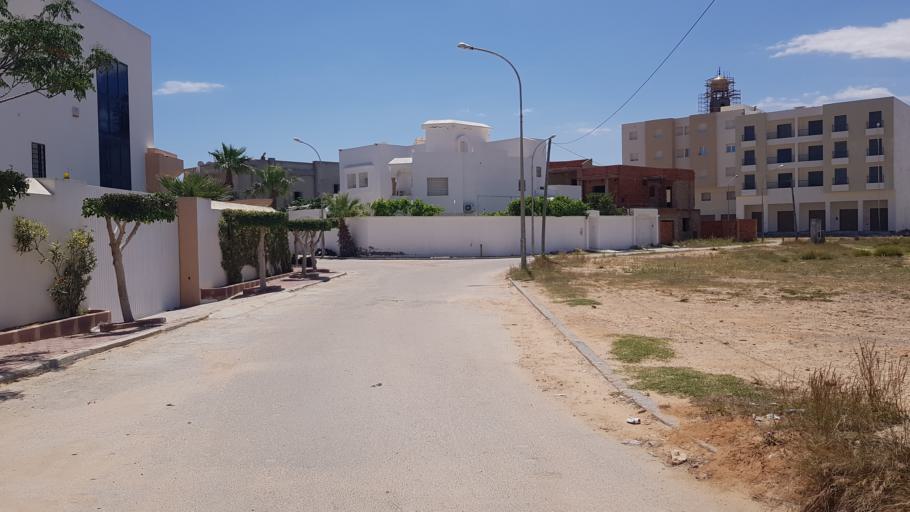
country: TN
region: Safaqis
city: Al Qarmadah
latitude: 34.8280
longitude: 10.7603
